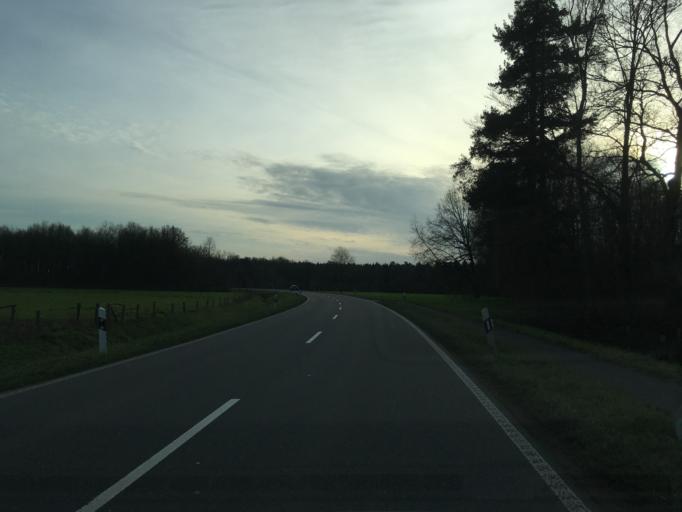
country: DE
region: North Rhine-Westphalia
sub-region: Regierungsbezirk Munster
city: Ahaus
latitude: 52.0214
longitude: 7.0233
